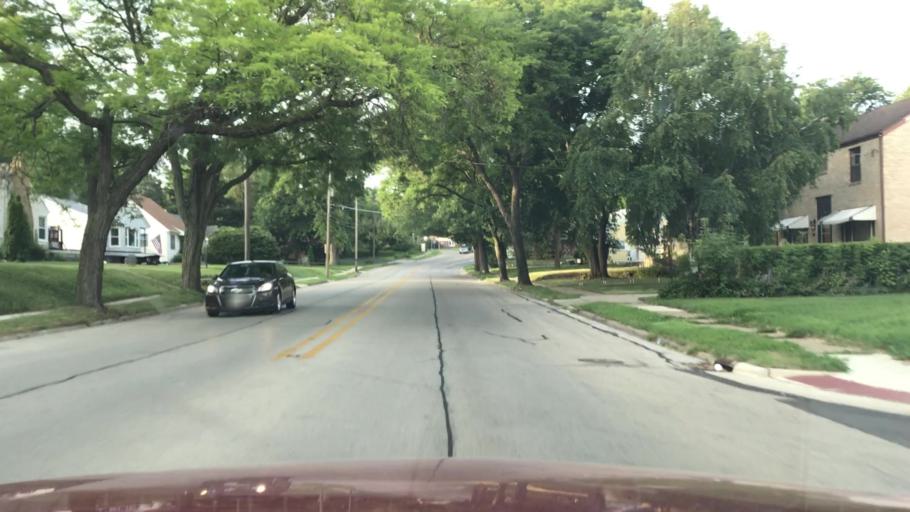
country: US
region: Illinois
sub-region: Winnebago County
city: Rockford
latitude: 42.2580
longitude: -89.0429
